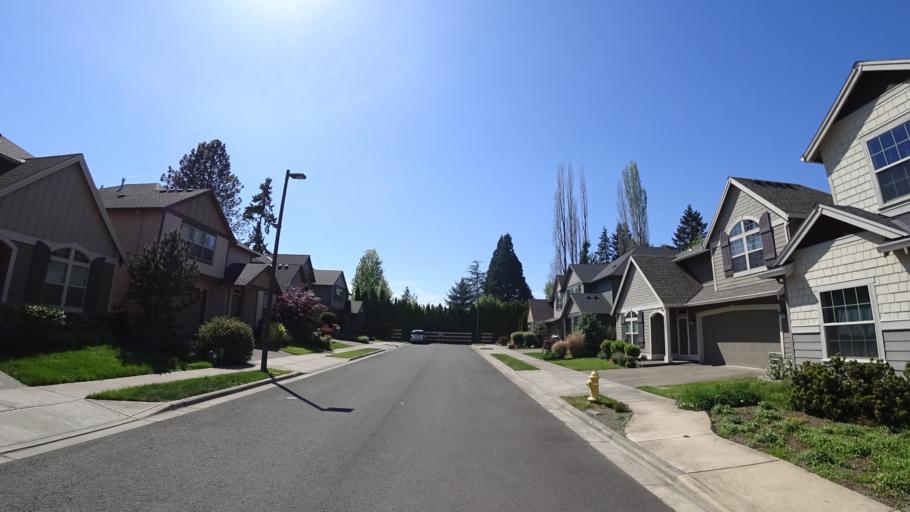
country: US
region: Oregon
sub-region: Washington County
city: Aloha
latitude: 45.4818
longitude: -122.8425
